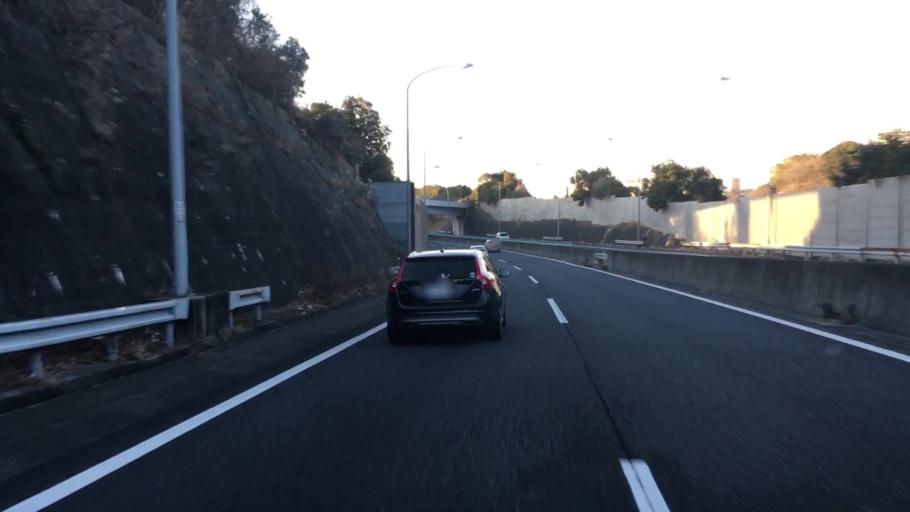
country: JP
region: Kanagawa
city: Kamakura
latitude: 35.3705
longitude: 139.5938
